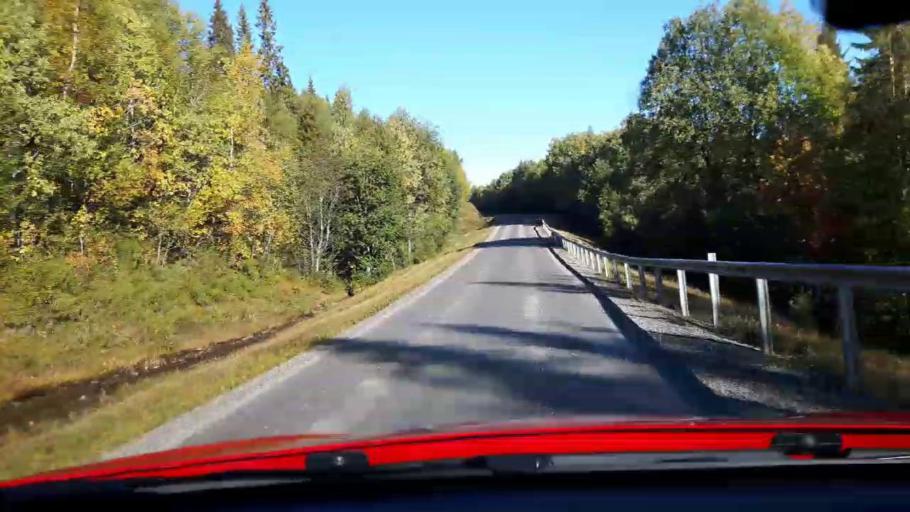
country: NO
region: Nord-Trondelag
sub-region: Lierne
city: Sandvika
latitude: 64.5705
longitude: 13.9032
